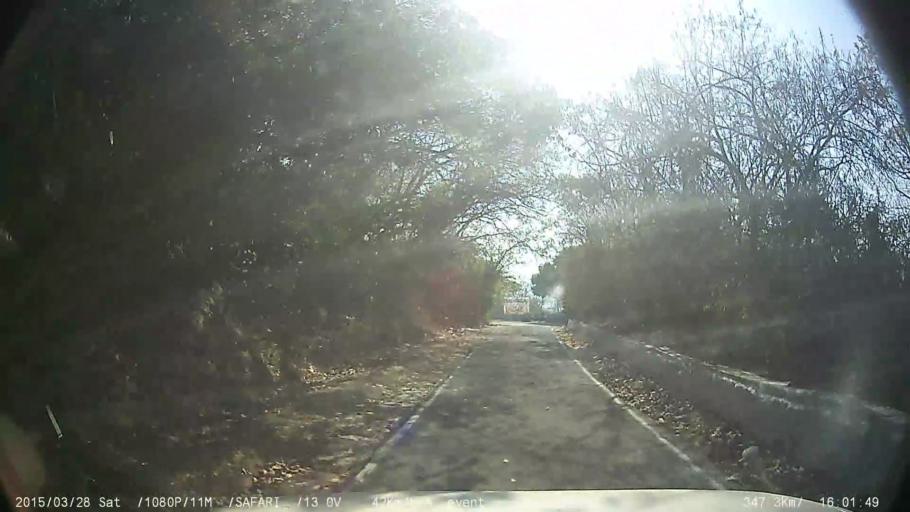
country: IN
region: Karnataka
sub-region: Mysore
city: Mysore
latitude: 12.2800
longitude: 76.6688
